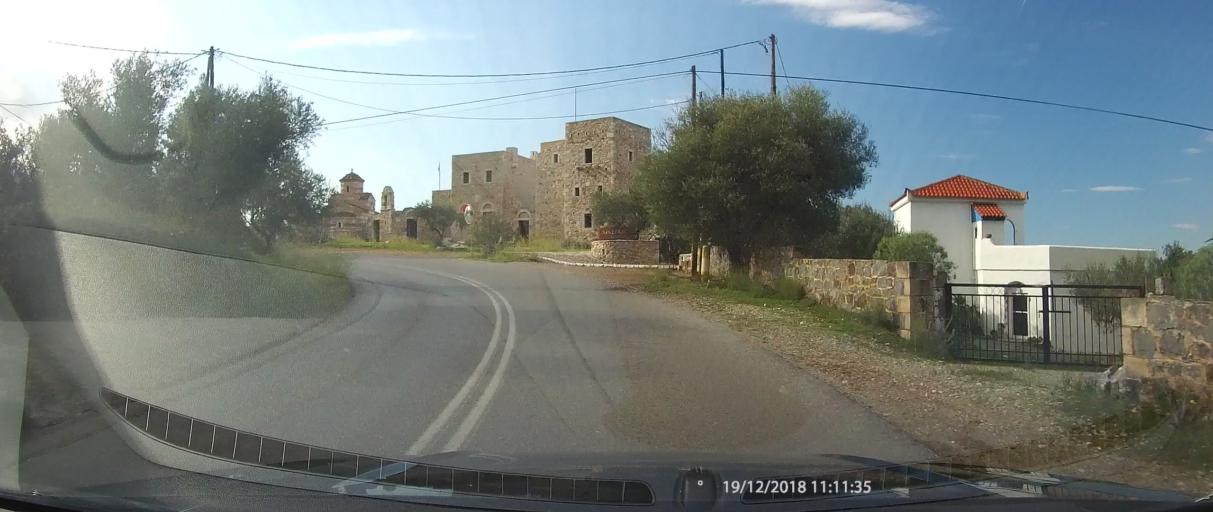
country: GR
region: Peloponnese
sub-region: Nomos Messinias
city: Kardamyli
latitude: 36.8191
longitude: 22.3015
